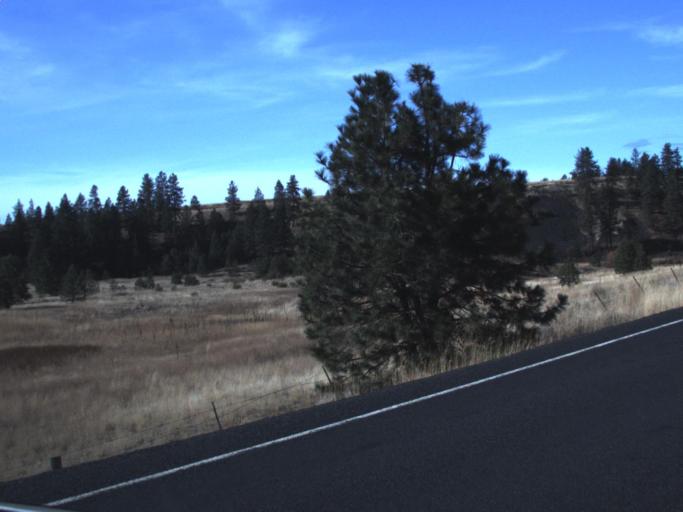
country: US
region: Washington
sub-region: Lincoln County
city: Davenport
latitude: 47.8142
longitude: -118.1817
